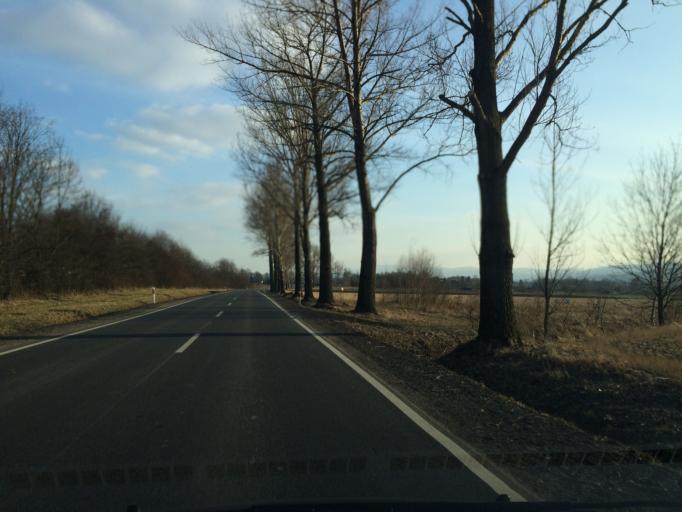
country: PL
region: Lower Silesian Voivodeship
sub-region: Powiat klodzki
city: Miedzylesie
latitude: 50.2239
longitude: 16.6784
